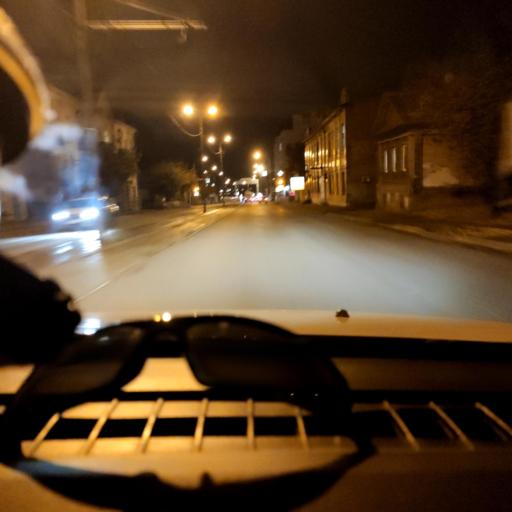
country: RU
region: Samara
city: Rozhdestveno
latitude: 53.1815
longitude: 50.0874
